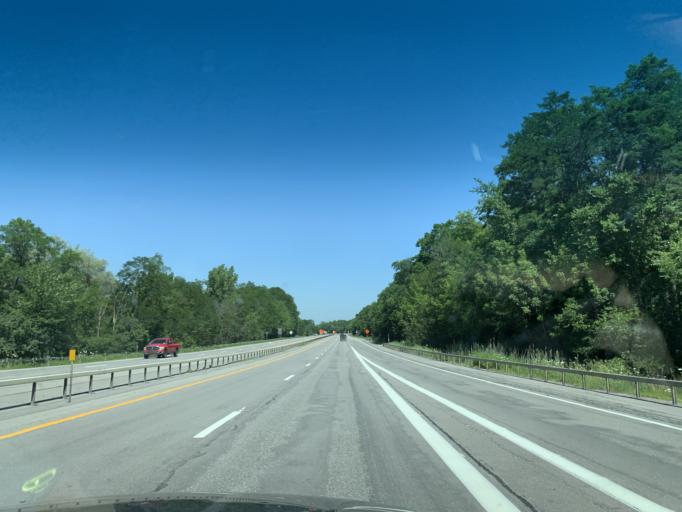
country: US
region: New York
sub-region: Oneida County
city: Chadwicks
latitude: 43.0088
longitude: -75.2542
